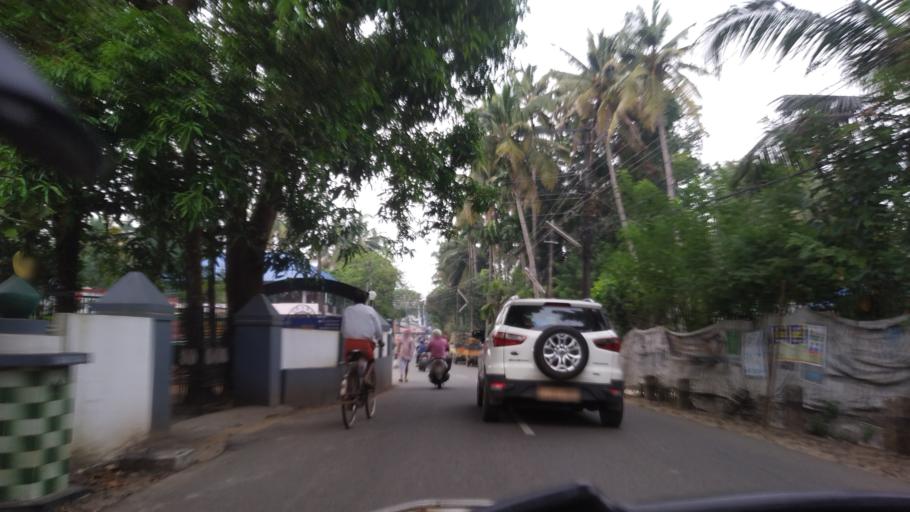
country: IN
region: Kerala
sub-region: Thrissur District
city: Kodungallur
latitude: 10.1426
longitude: 76.2172
